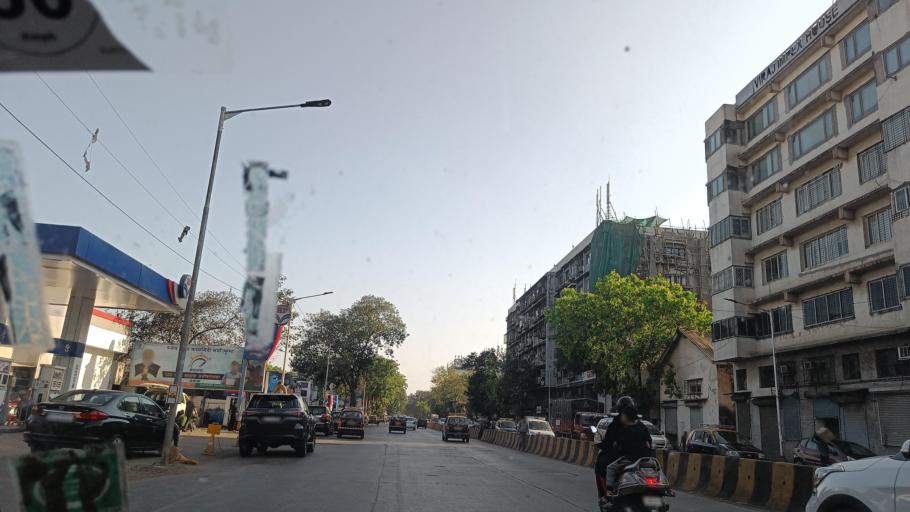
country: IN
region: Maharashtra
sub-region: Raigarh
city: Uran
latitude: 18.9518
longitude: 72.8414
